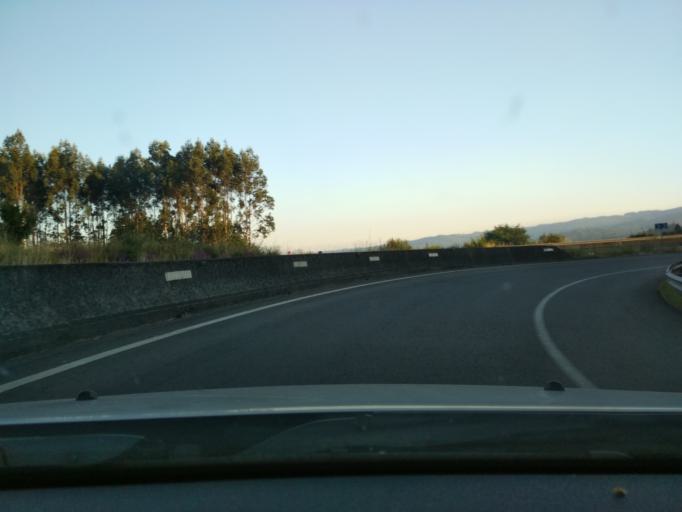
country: ES
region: Galicia
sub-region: Provincia da Coruna
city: Santiago de Compostela
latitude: 42.8554
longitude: -8.5663
